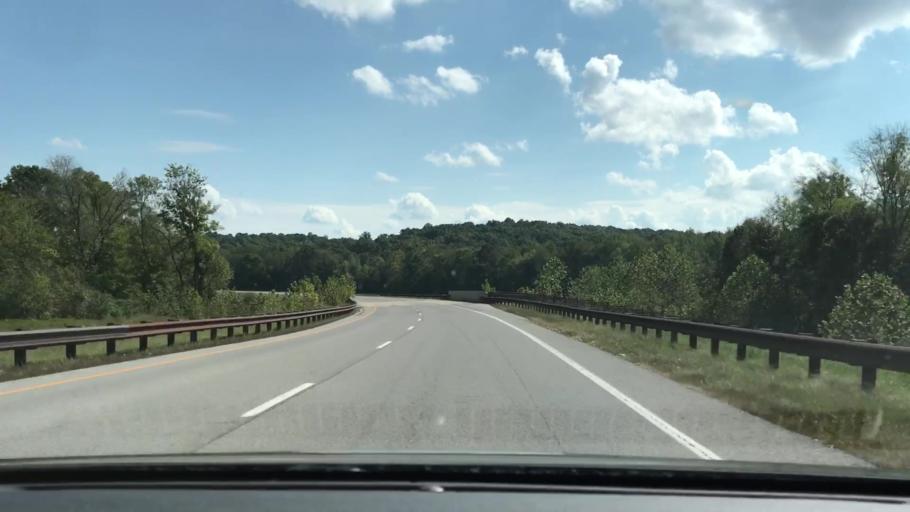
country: US
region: Kentucky
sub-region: Trigg County
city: Cadiz
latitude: 36.7846
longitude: -88.0228
